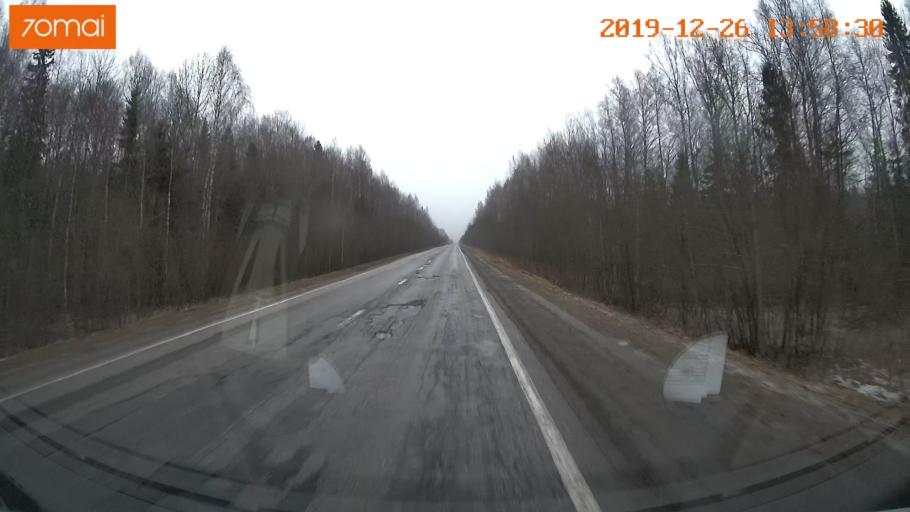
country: RU
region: Jaroslavl
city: Poshekhon'ye
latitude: 58.5735
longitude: 38.7022
